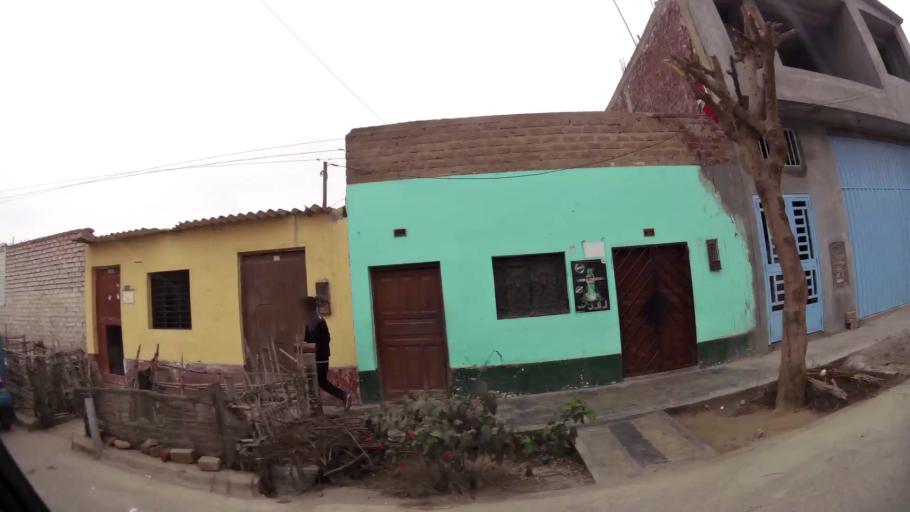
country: PE
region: Lima
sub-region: Barranca
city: Barranca
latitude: -10.7450
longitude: -77.7571
